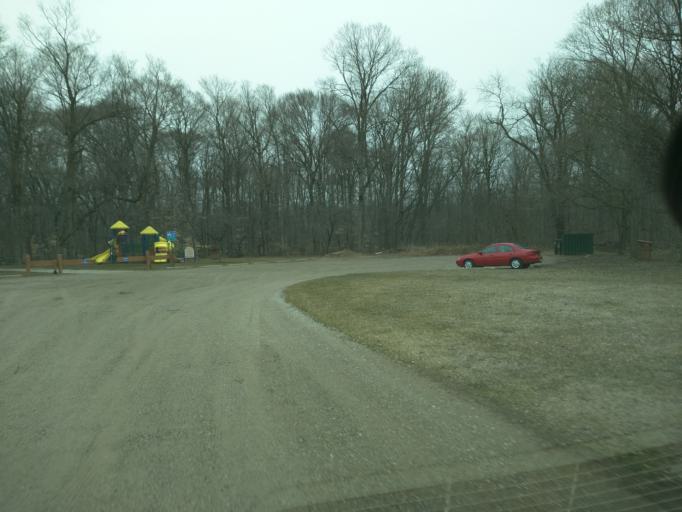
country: US
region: Michigan
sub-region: Ingham County
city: Edgemont Park
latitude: 42.7569
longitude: -84.6093
